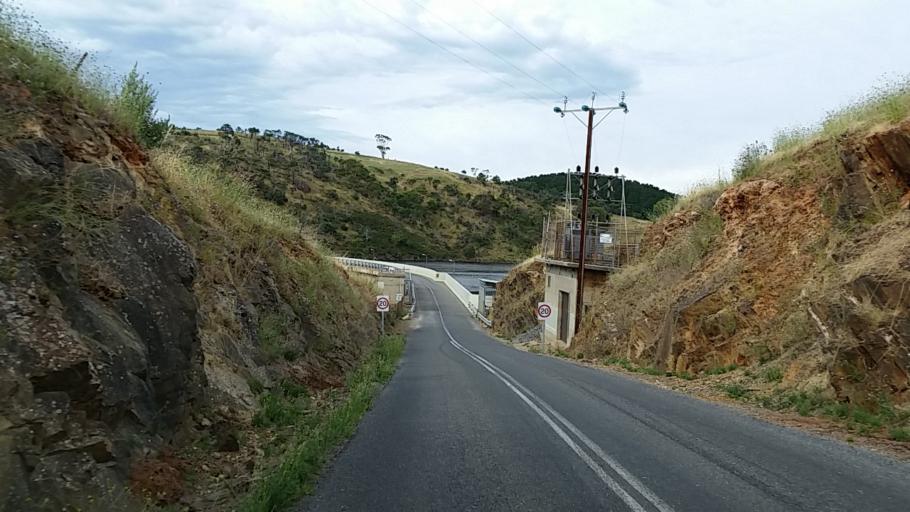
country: AU
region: South Australia
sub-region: Yankalilla
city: Normanville
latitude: -35.4019
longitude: 138.4194
